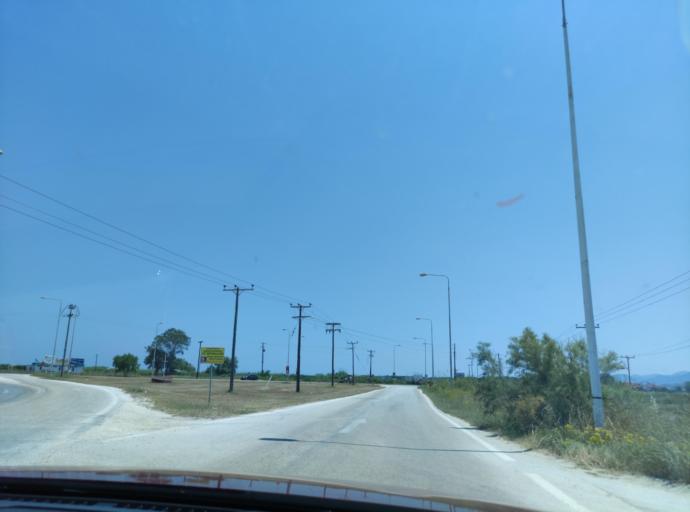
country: GR
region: East Macedonia and Thrace
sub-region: Nomos Kavalas
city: Keramoti
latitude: 40.8691
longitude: 24.7040
